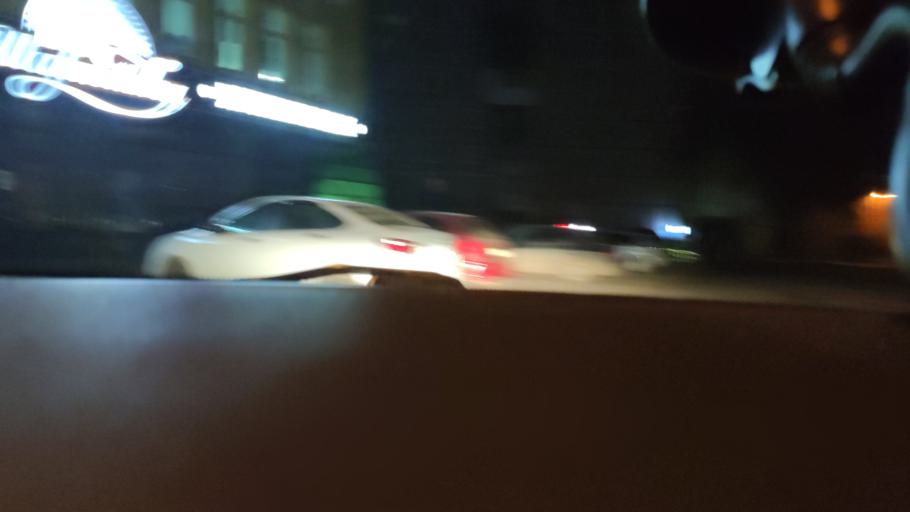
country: RU
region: Perm
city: Perm
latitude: 58.0225
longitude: 56.2989
